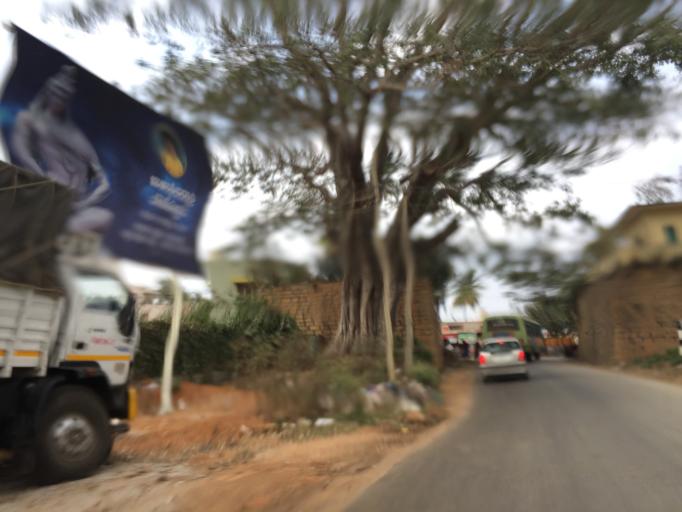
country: IN
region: Karnataka
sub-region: Chikkaballapur
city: Chik Ballapur
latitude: 13.4276
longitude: 77.7228
